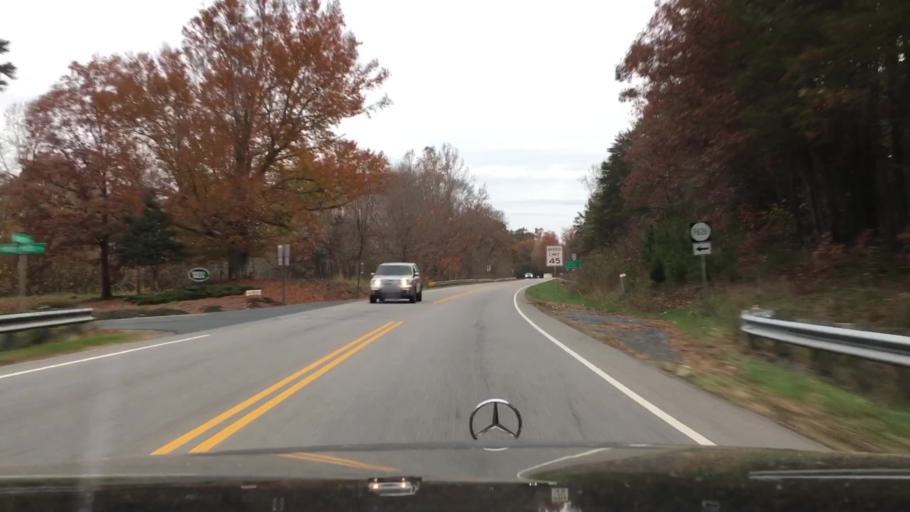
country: US
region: Virginia
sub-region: Campbell County
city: Altavista
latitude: 37.1300
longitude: -79.3072
